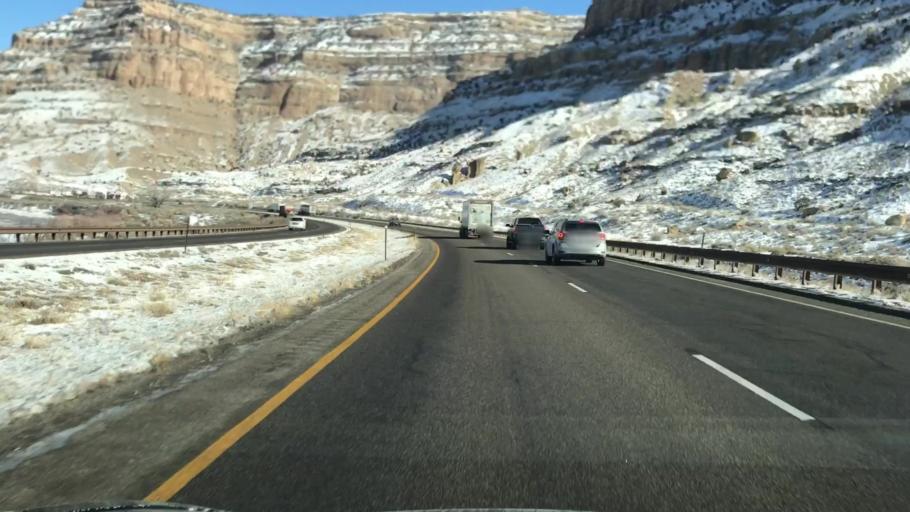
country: US
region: Colorado
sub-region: Mesa County
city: Palisade
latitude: 39.1518
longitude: -108.3038
